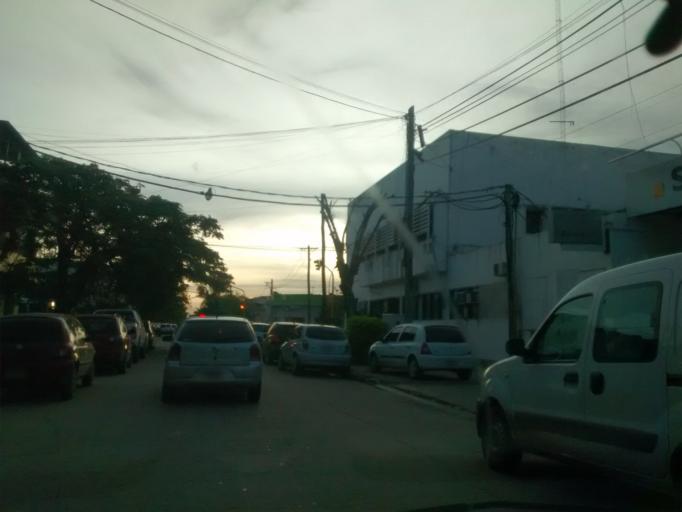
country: AR
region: Chaco
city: Resistencia
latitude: -27.4404
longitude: -58.9978
